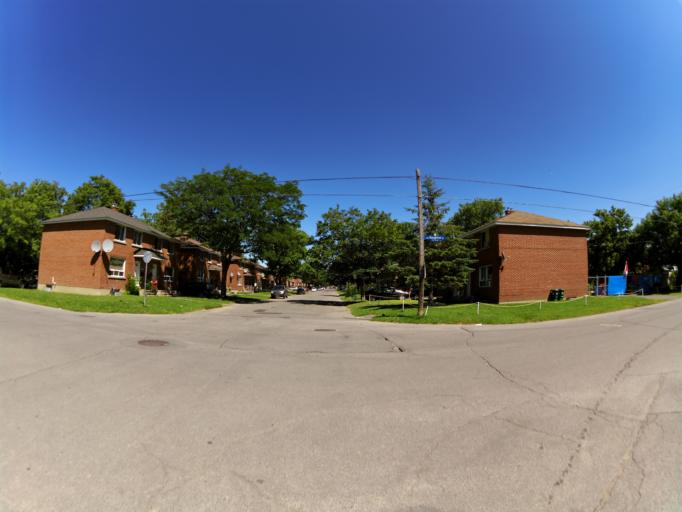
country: CA
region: Ontario
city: Ottawa
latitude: 45.4260
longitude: -75.6500
